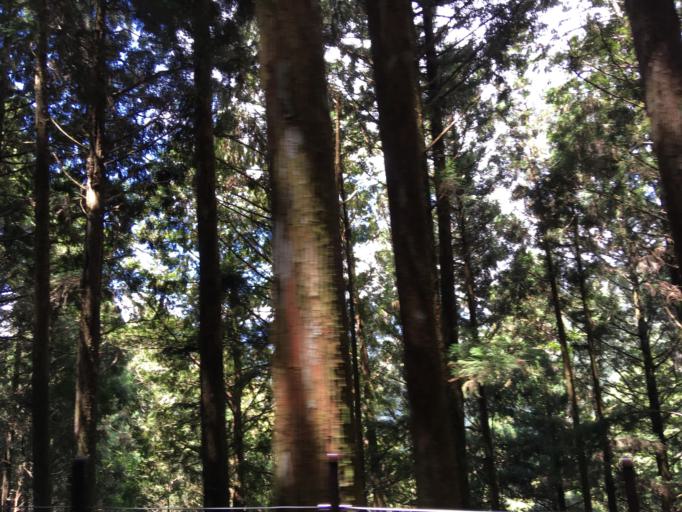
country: TW
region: Taiwan
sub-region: Yilan
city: Yilan
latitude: 24.4774
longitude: 121.5345
